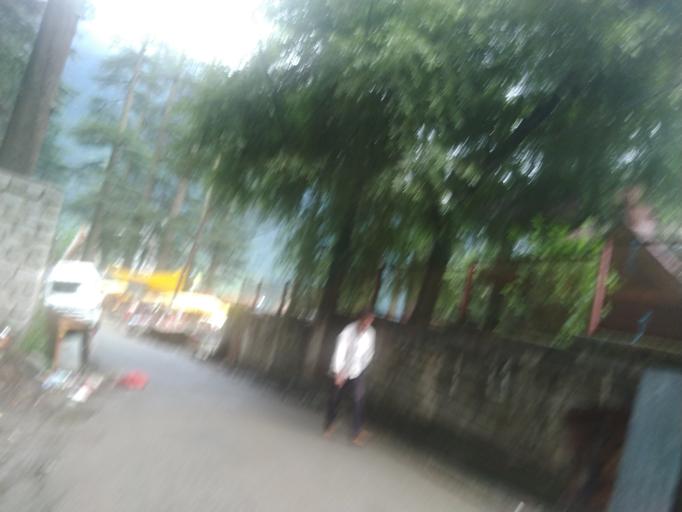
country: IN
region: Himachal Pradesh
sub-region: Kulu
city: Manali
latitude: 32.2467
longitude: 77.1802
